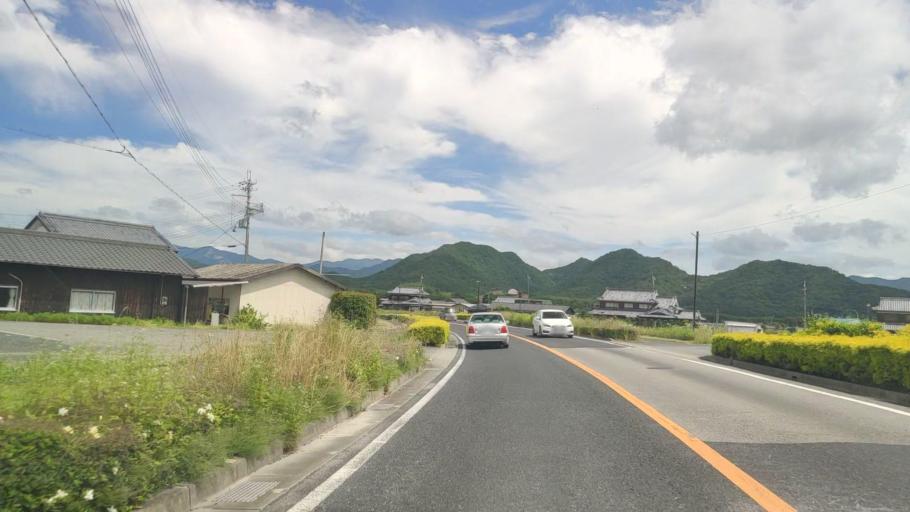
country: JP
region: Hyogo
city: Nishiwaki
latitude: 35.0318
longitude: 134.9410
